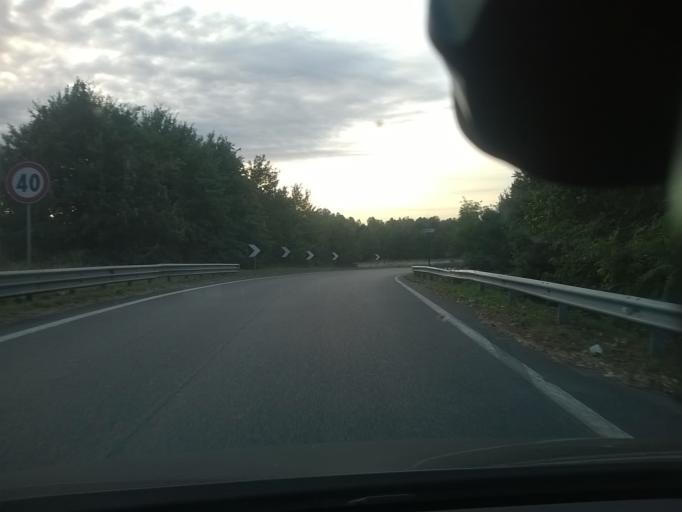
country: IT
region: Lombardy
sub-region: Provincia di Bergamo
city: Grassobbio
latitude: 45.6675
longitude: 9.7370
